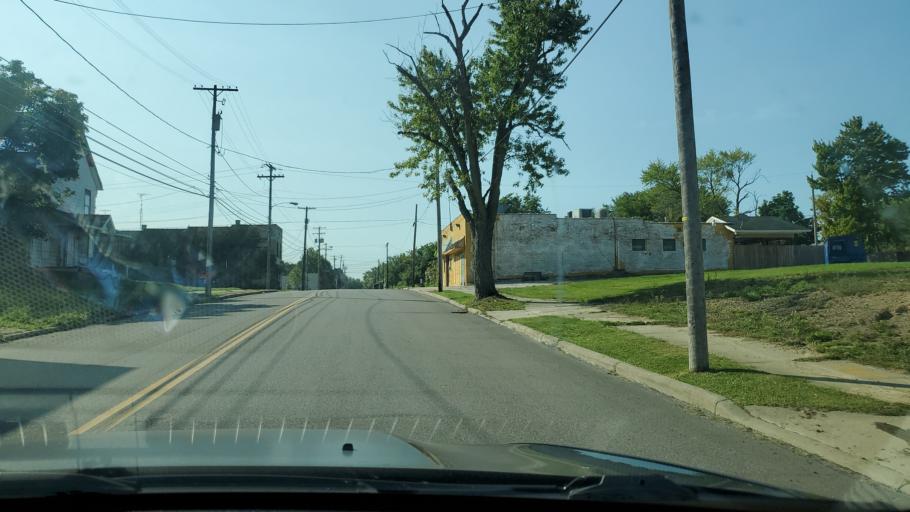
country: US
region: Ohio
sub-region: Mahoning County
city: Youngstown
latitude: 41.1108
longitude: -80.6828
